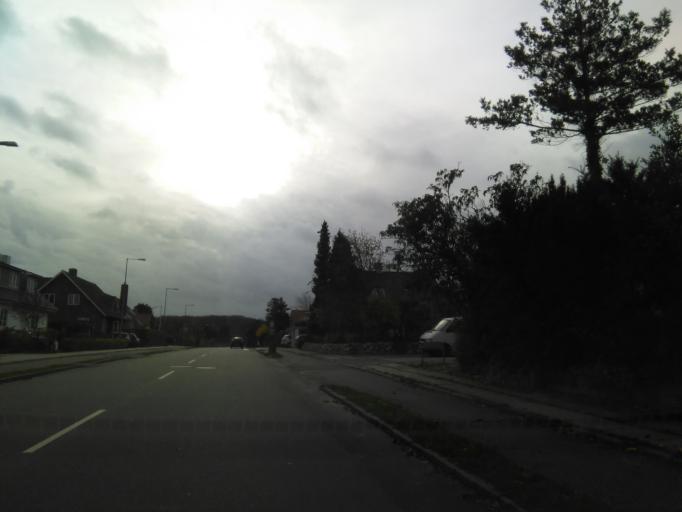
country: DK
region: Central Jutland
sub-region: Arhus Kommune
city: Arhus
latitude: 56.1891
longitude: 10.2280
